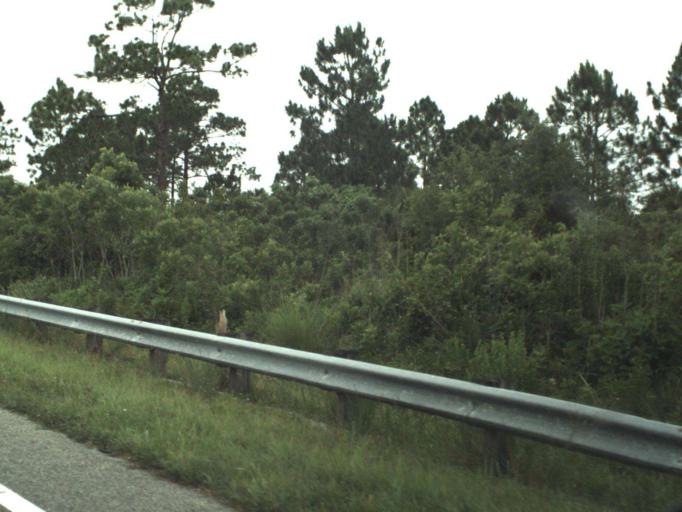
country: US
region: Florida
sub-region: Brevard County
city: Titusville
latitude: 28.5509
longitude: -80.8742
